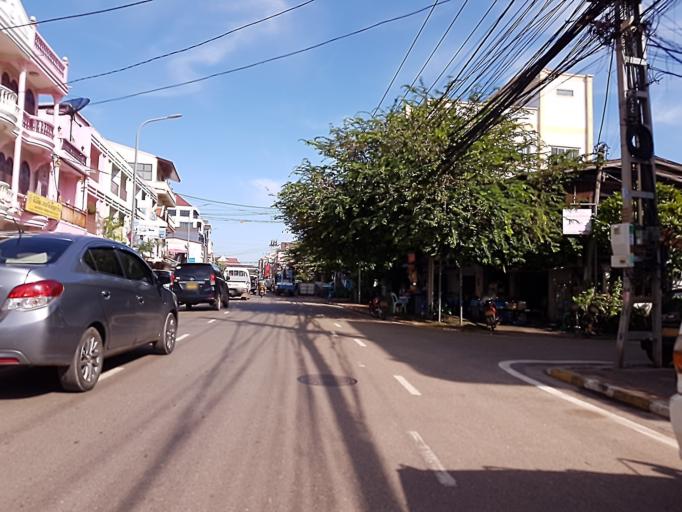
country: LA
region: Vientiane
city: Vientiane
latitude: 17.9589
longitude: 102.6177
